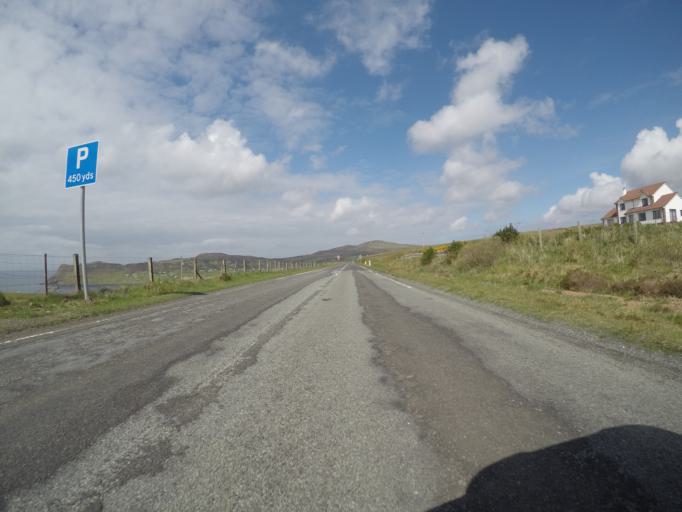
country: GB
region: Scotland
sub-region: Highland
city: Portree
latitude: 57.5747
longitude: -6.3652
